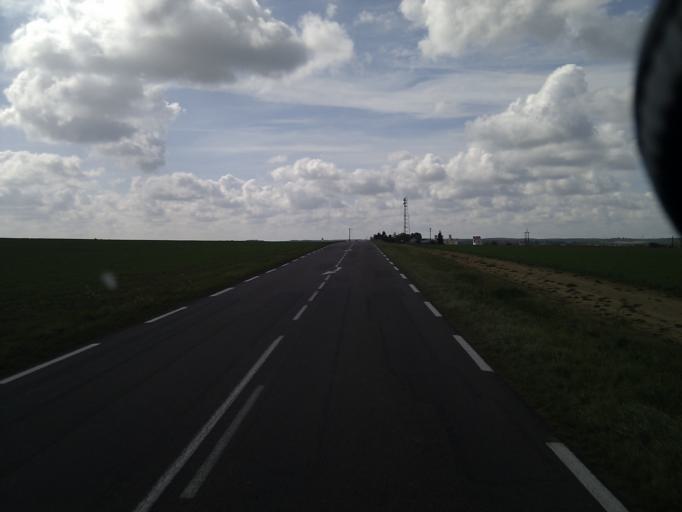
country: FR
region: Bourgogne
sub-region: Departement de la Cote-d'Or
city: Chatillon-sur-Seine
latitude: 47.8764
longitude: 4.5865
